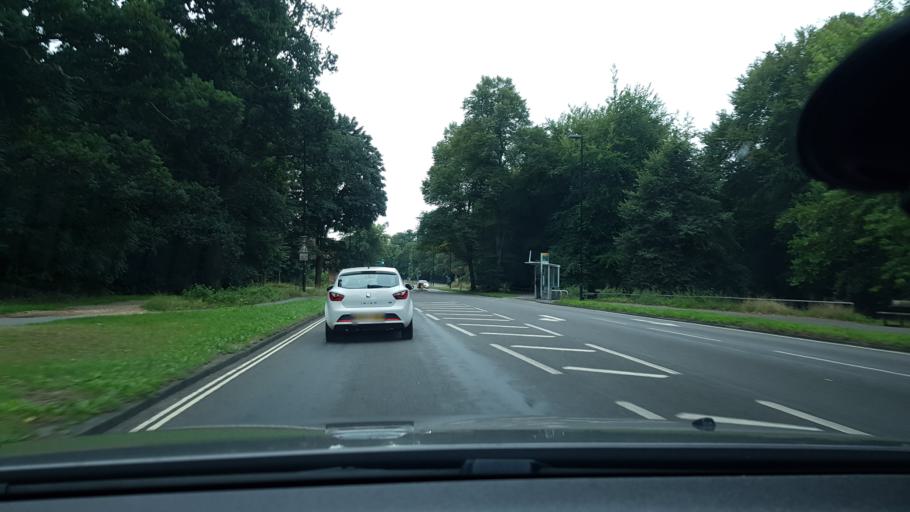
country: GB
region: England
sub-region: Southampton
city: Southampton
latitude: 50.9231
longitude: -1.4051
